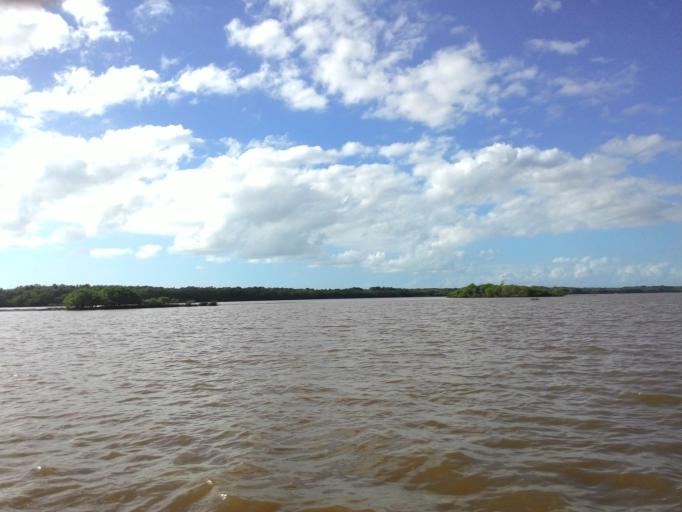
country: BR
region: Sao Paulo
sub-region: Pariquera-Acu
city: Pariquera Acu
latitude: -24.8611
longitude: -47.7680
